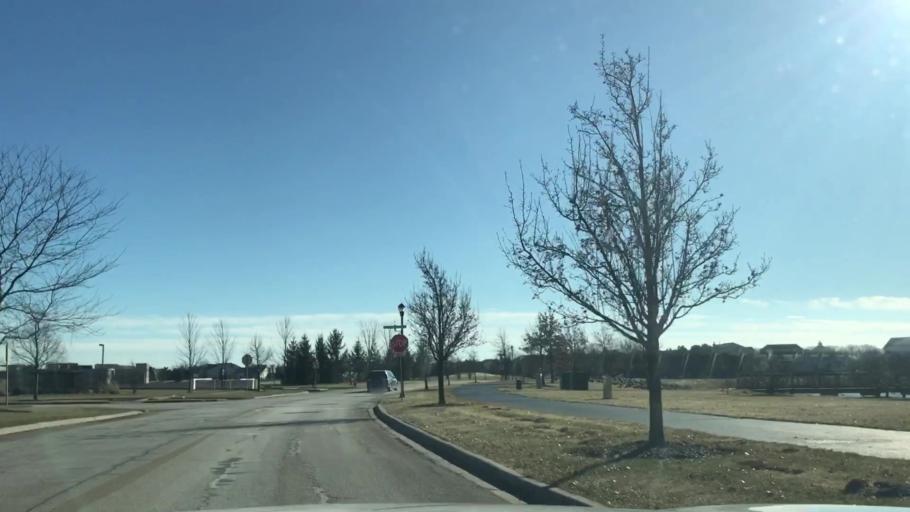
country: US
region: Illinois
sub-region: Kane County
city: Pingree Grove
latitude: 42.0836
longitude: -88.4320
